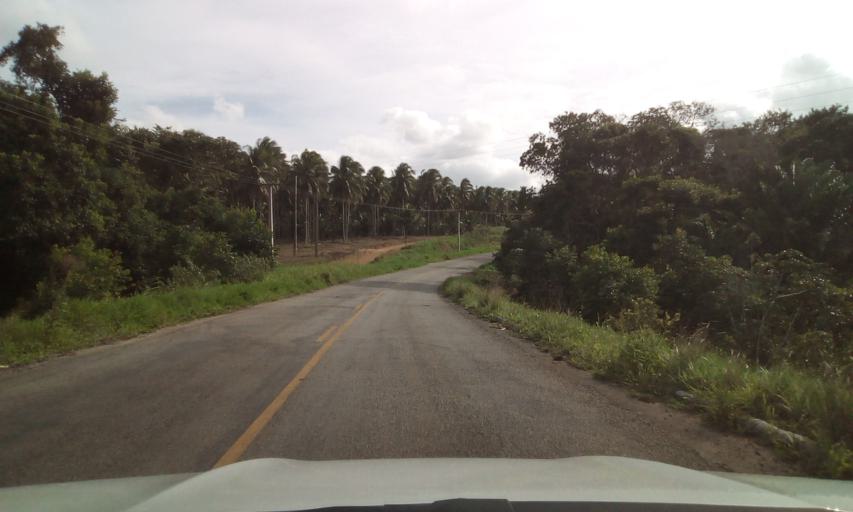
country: BR
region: Paraiba
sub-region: Cabedelo
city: Cabedelo
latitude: -6.9627
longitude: -34.9450
